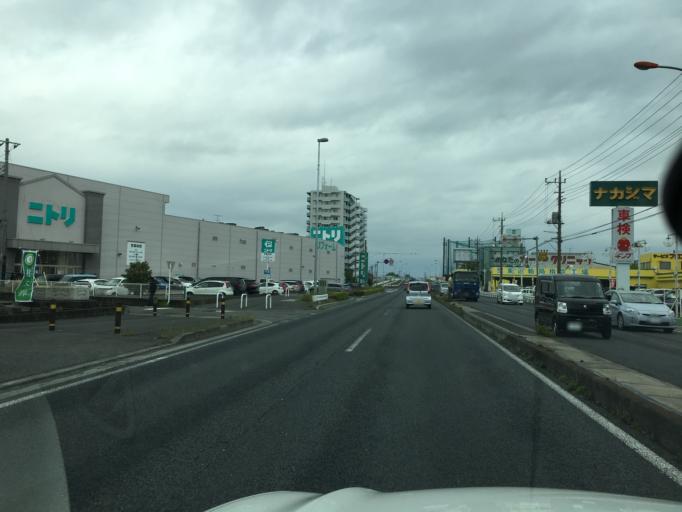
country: JP
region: Saitama
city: Koshigaya
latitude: 35.8564
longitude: 139.7828
